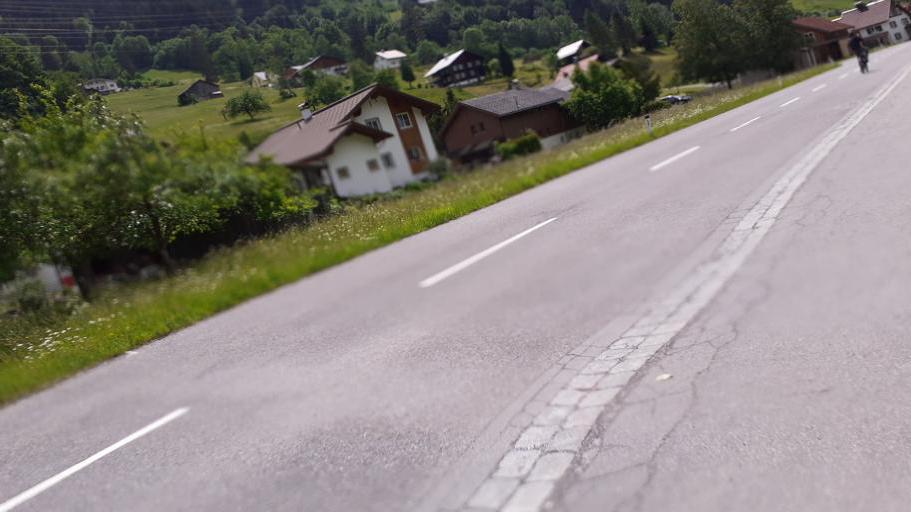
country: AT
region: Vorarlberg
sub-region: Politischer Bezirk Bludenz
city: Dalaas
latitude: 47.1224
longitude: 9.9957
